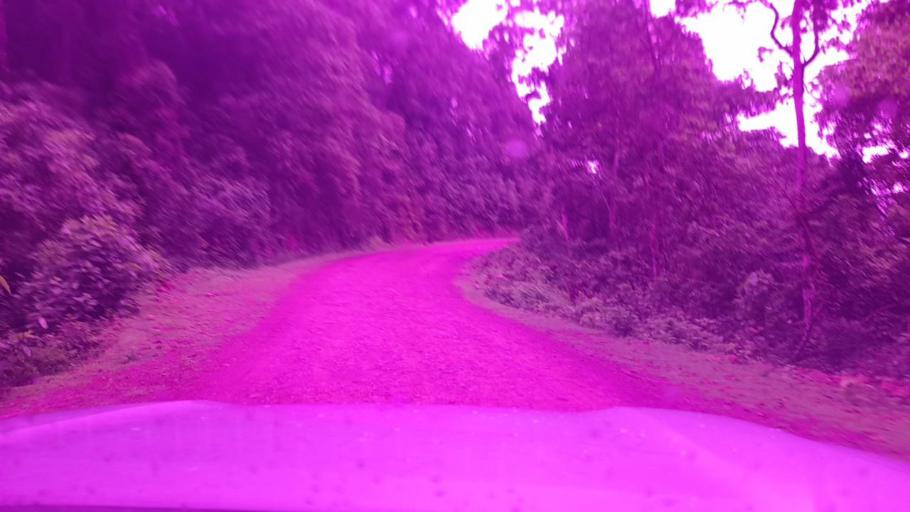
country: ET
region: Southern Nations, Nationalities, and People's Region
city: Bonga
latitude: 7.5089
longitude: 36.0657
